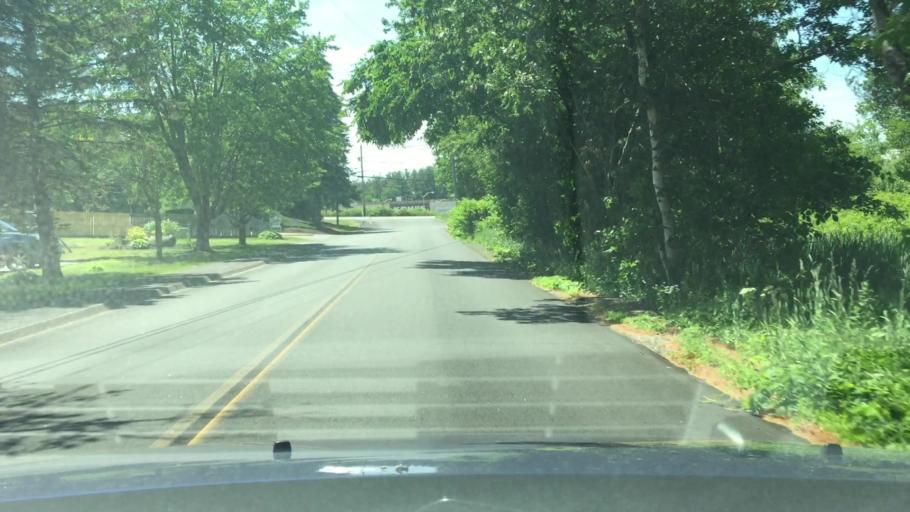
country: US
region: New Hampshire
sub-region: Rockingham County
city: Plaistow
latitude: 42.8209
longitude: -71.1024
